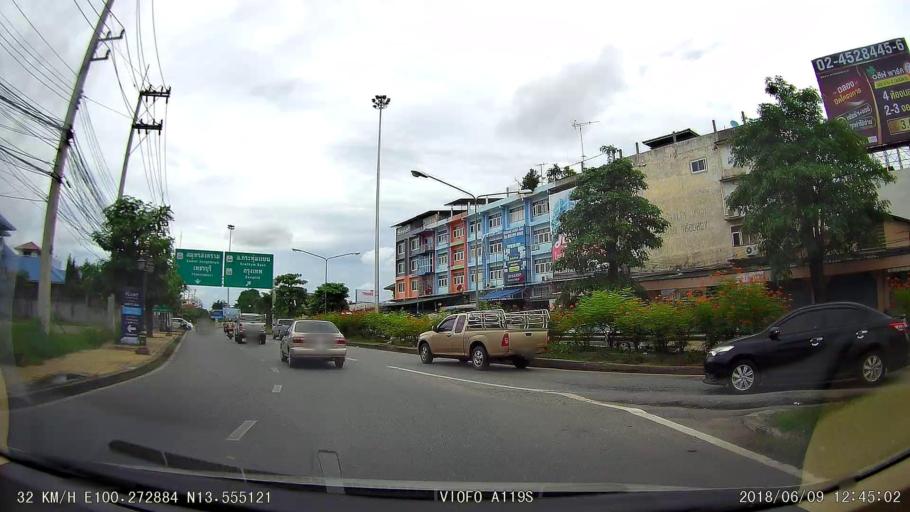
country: TH
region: Samut Sakhon
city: Samut Sakhon
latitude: 13.5554
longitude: 100.2710
